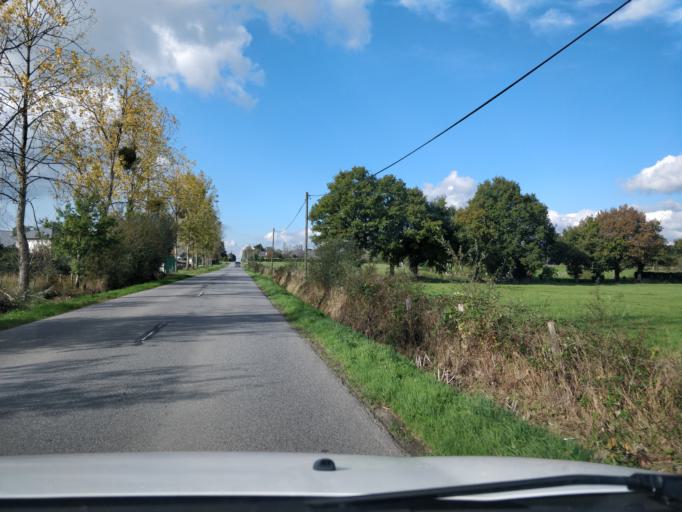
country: FR
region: Brittany
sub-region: Departement d'Ille-et-Vilaine
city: La Bouexiere
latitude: 48.1709
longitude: -1.4299
